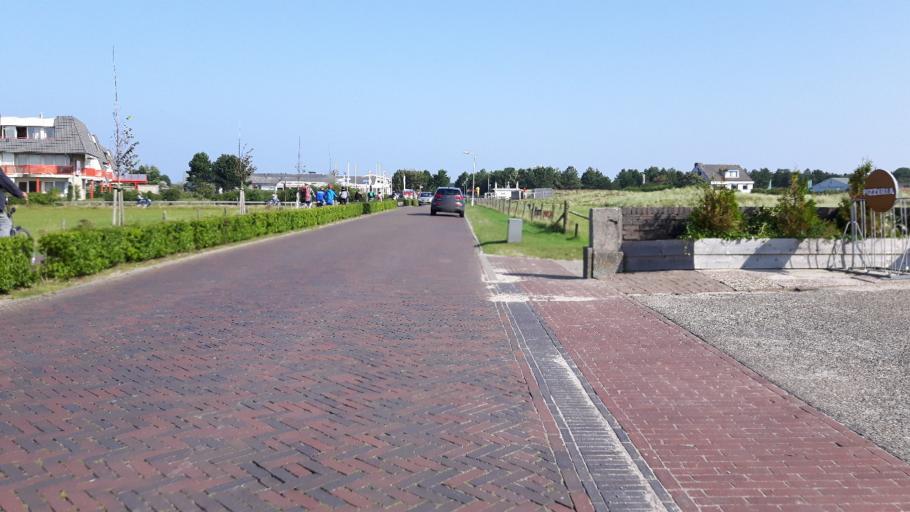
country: NL
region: Friesland
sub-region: Gemeente Ameland
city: Nes
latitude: 53.4520
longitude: 5.8018
